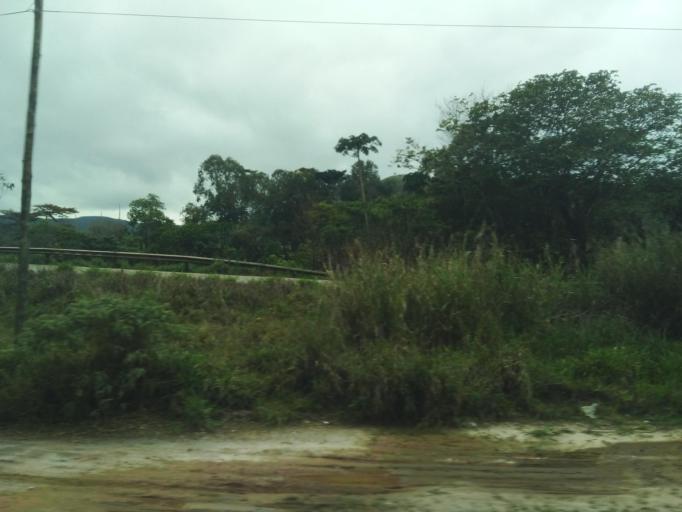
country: BR
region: Minas Gerais
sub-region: Rio Piracicaba
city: Rio Piracicaba
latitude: -19.9384
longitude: -43.1782
